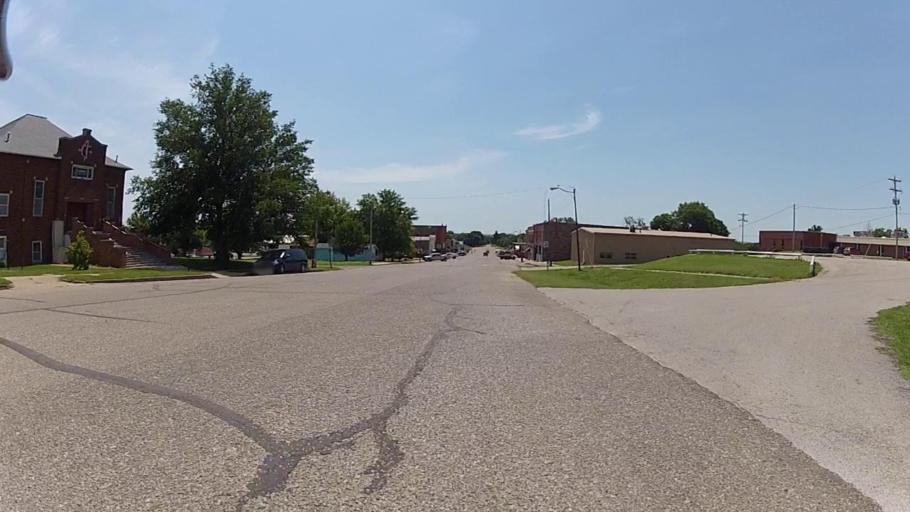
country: US
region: Kansas
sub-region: Chautauqua County
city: Sedan
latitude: 37.1063
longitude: -96.5003
